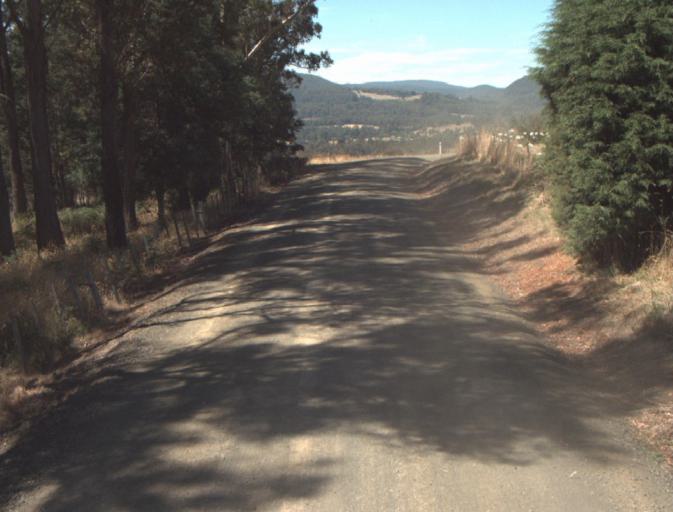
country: AU
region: Tasmania
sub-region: Launceston
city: Mayfield
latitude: -41.2470
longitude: 147.1341
